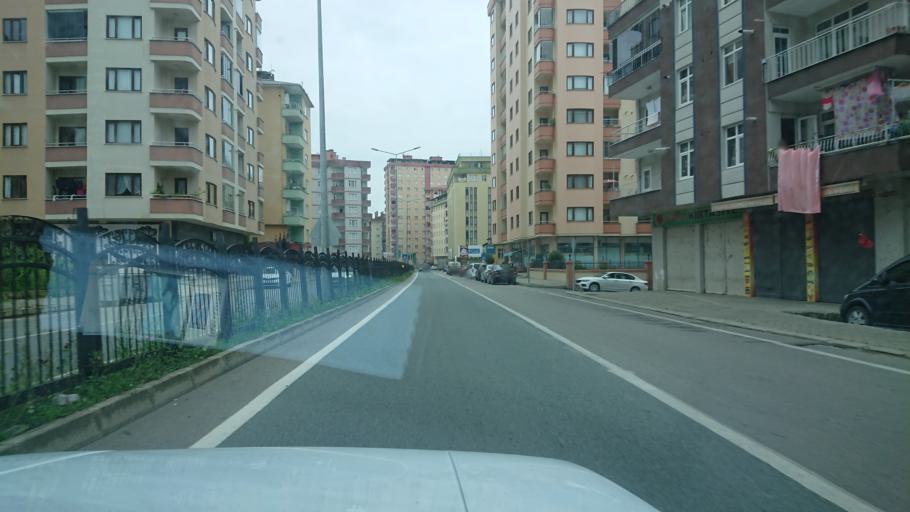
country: TR
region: Rize
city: Rize
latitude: 41.0239
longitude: 40.5418
